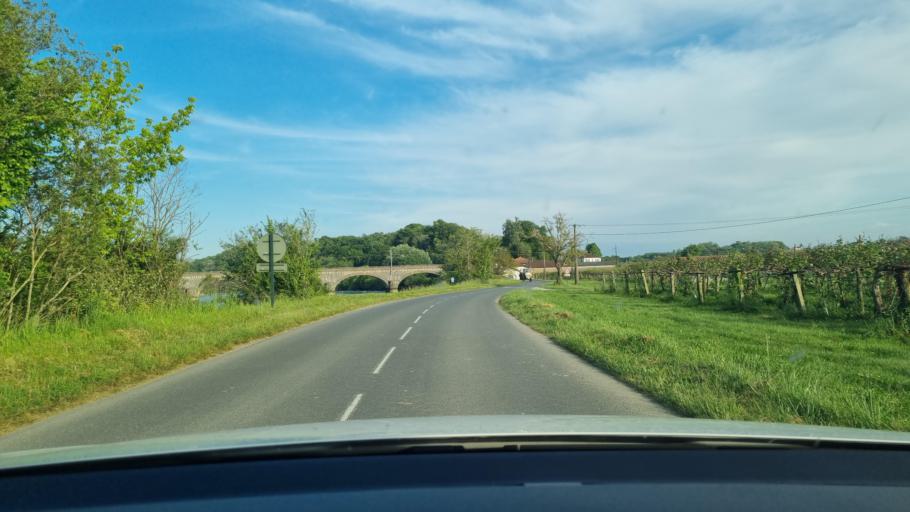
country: FR
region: Aquitaine
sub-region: Departement des Landes
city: Peyrehorade
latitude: 43.5401
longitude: -1.1621
